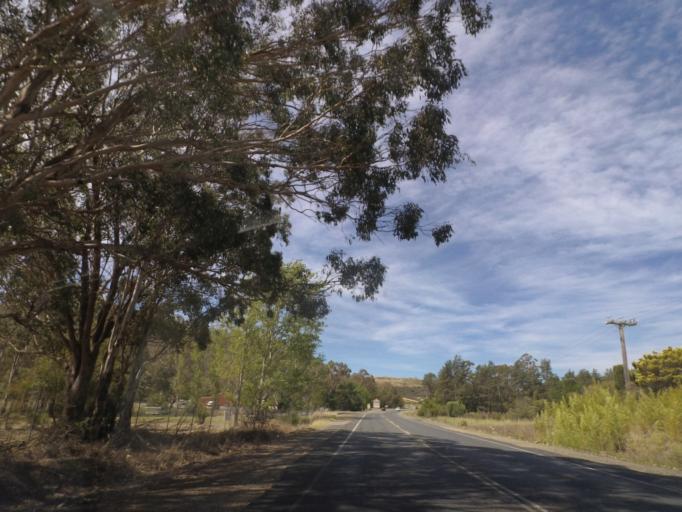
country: AU
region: New South Wales
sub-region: Wollondilly
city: Picton
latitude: -34.1643
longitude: 150.6340
